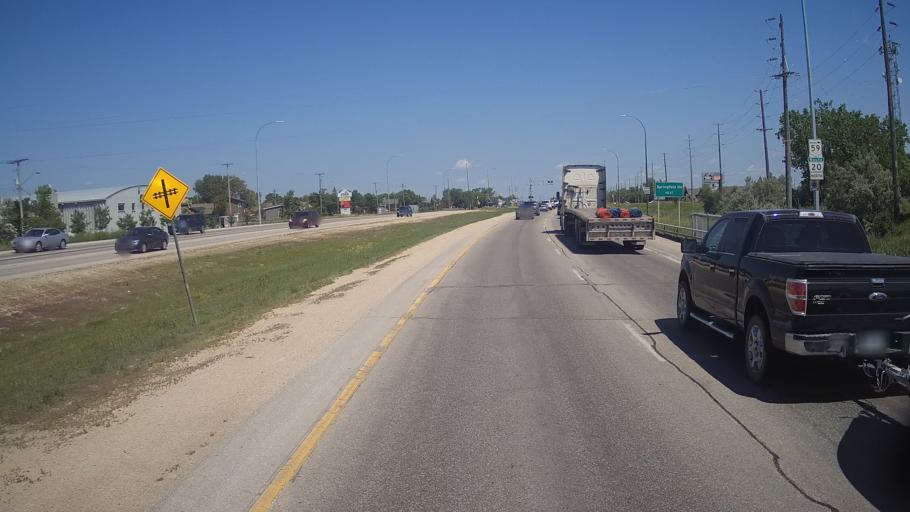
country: CA
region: Manitoba
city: Winnipeg
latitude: 49.9284
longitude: -97.0469
